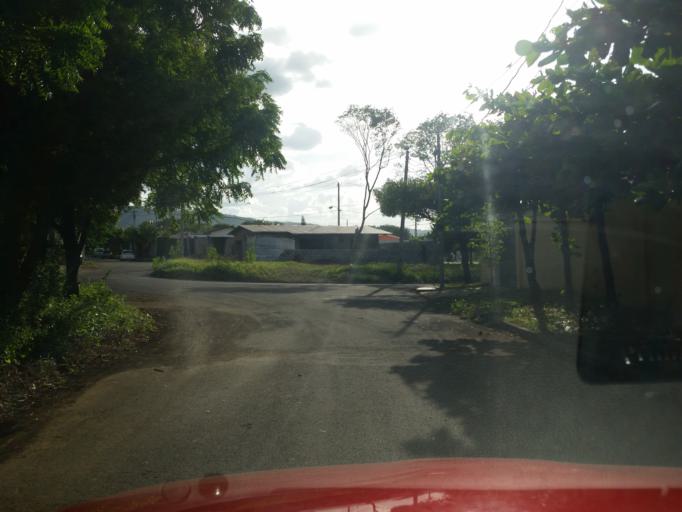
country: NI
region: Masaya
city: Ticuantepe
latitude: 12.0548
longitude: -86.1911
